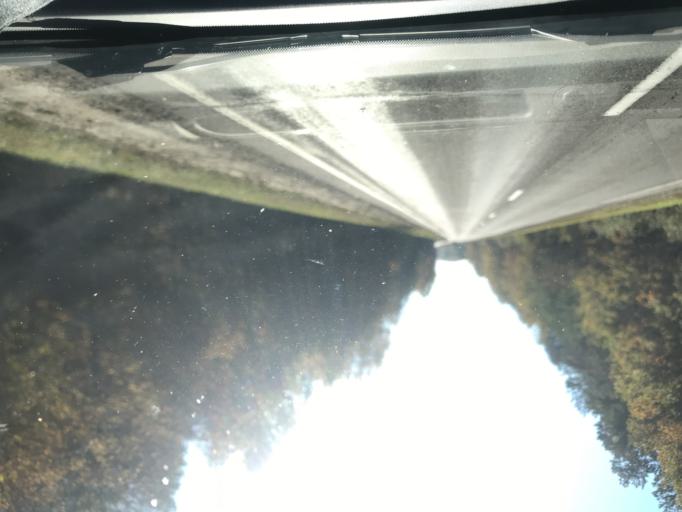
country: BY
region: Gomel
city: Kastsyukowka
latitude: 52.4278
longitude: 30.8278
